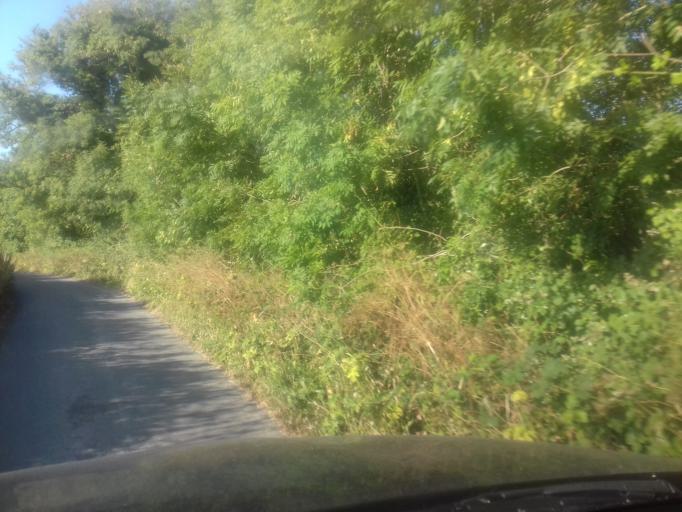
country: IE
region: Leinster
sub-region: Fingal County
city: Blanchardstown
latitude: 53.4335
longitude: -6.3686
